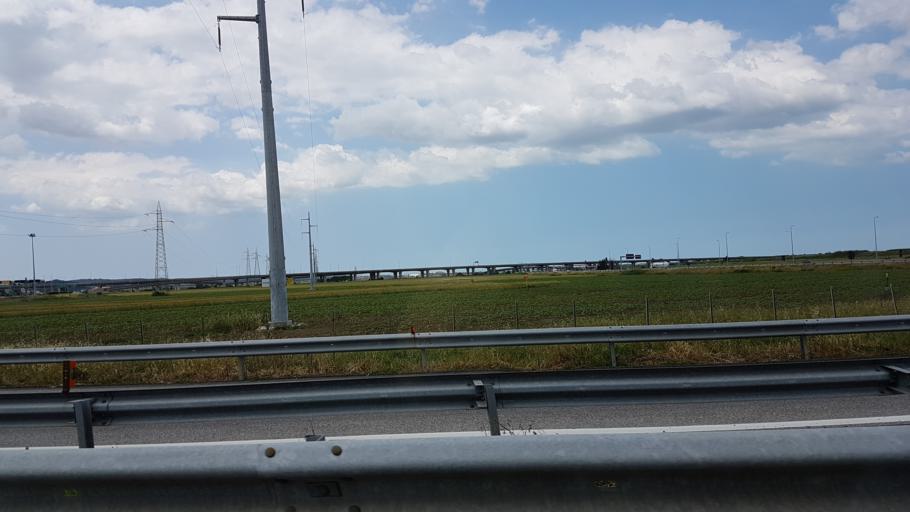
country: IT
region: Tuscany
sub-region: Provincia di Livorno
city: Vicarello
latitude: 43.6177
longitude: 10.4483
